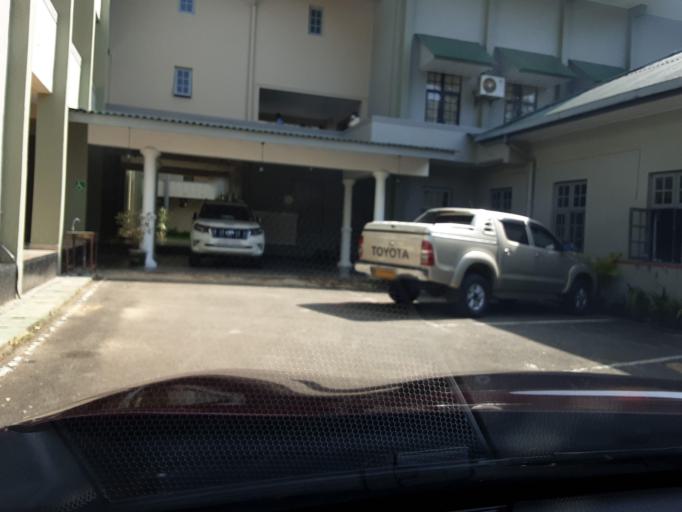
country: LK
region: Uva
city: Badulla
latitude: 6.9505
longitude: 81.1256
